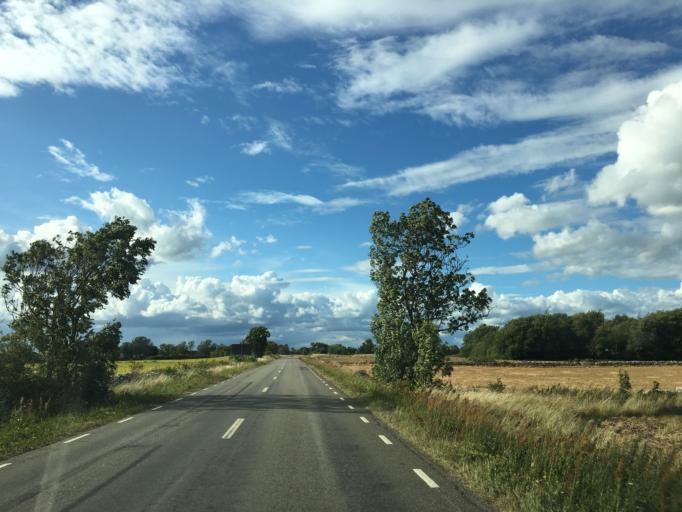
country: SE
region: Kalmar
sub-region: Morbylanga Kommun
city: Moerbylanga
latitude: 56.4387
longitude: 16.4315
